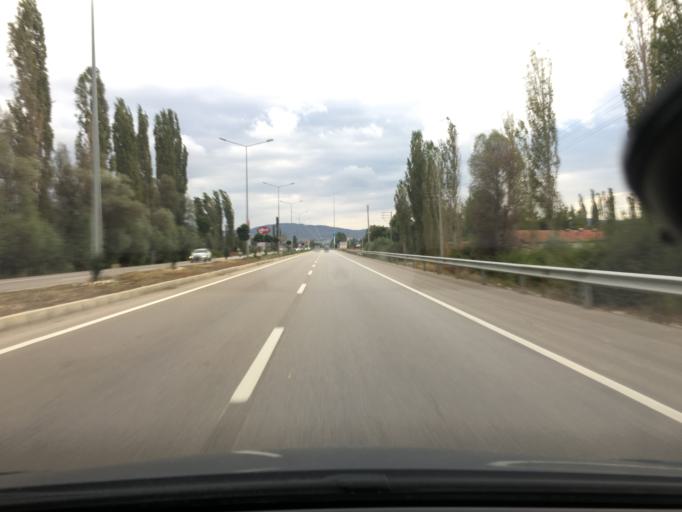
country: TR
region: Afyonkarahisar
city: Sincanli
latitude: 38.7651
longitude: 30.3657
